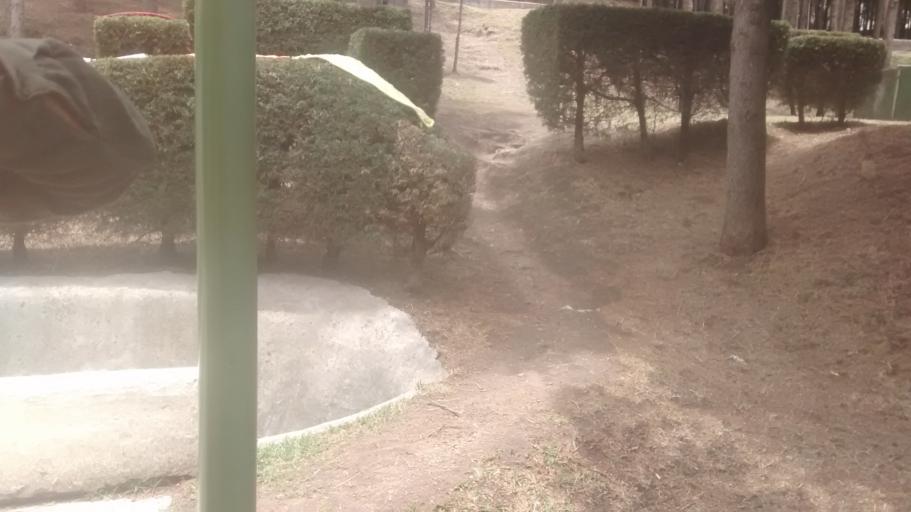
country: MX
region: Mexico
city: San Buenaventura
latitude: 19.2830
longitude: -99.6795
